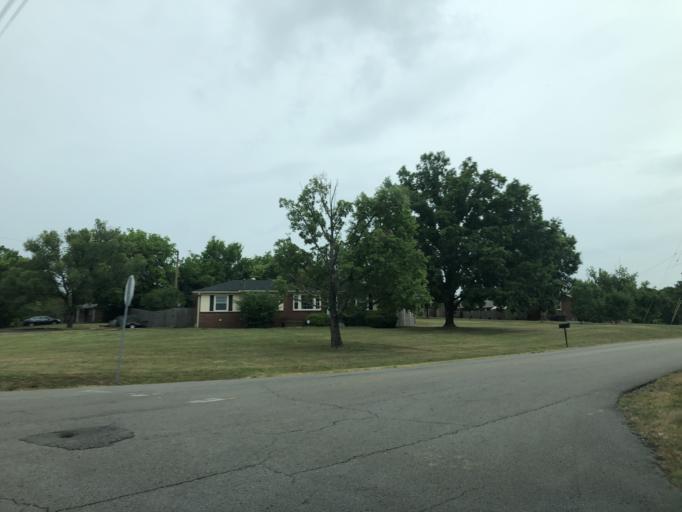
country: US
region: Tennessee
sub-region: Davidson County
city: Goodlettsville
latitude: 36.2610
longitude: -86.7655
